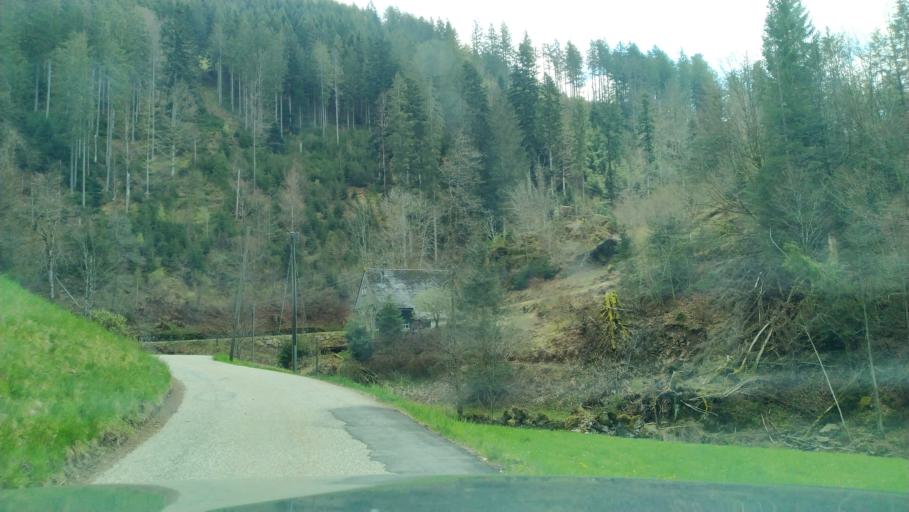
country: DE
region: Baden-Wuerttemberg
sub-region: Freiburg Region
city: Sankt Margen
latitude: 48.0223
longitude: 8.1246
